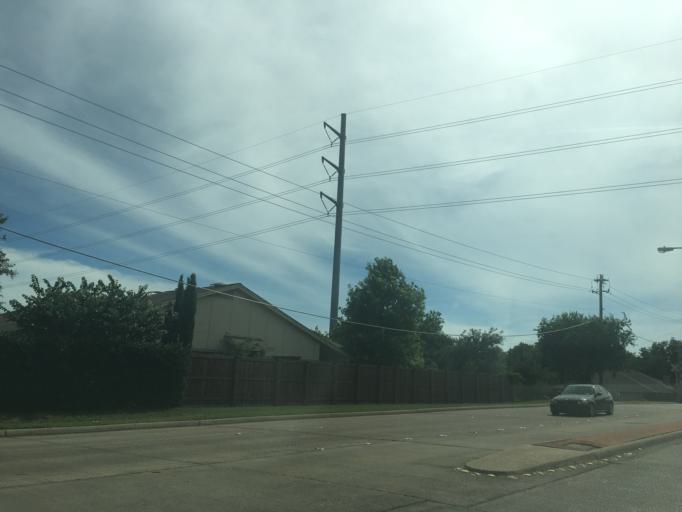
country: US
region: Texas
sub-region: Dallas County
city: Richardson
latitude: 32.9313
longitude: -96.7122
